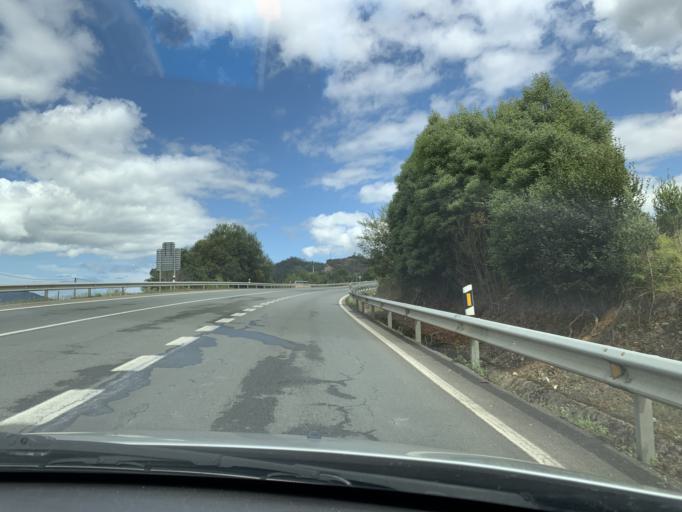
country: ES
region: Galicia
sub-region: Provincia de Lugo
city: Mondonedo
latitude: 43.4502
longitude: -7.3411
